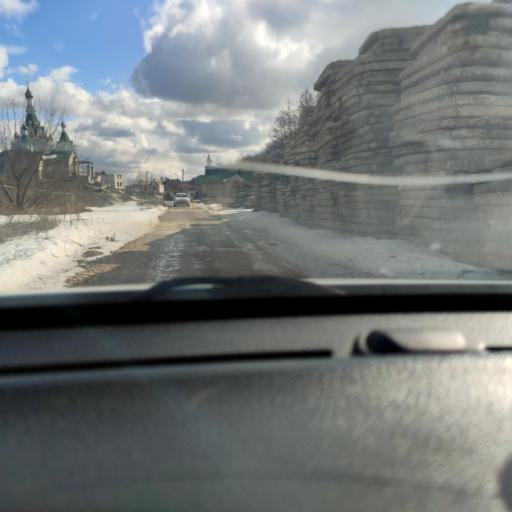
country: RU
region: Voronezj
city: Novaya Usman'
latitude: 51.6829
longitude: 39.3926
